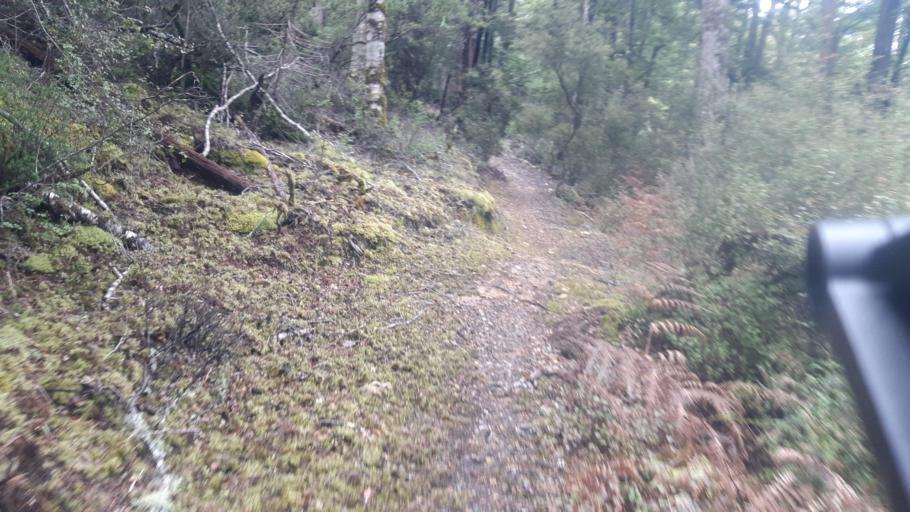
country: NZ
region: Tasman
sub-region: Tasman District
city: Wakefield
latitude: -41.7593
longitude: 172.8058
